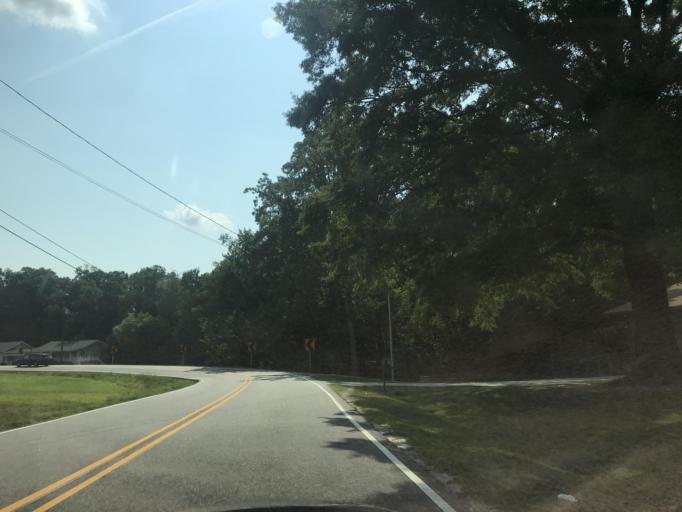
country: US
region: North Carolina
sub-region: Wake County
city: Morrisville
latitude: 35.8308
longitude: -78.8626
